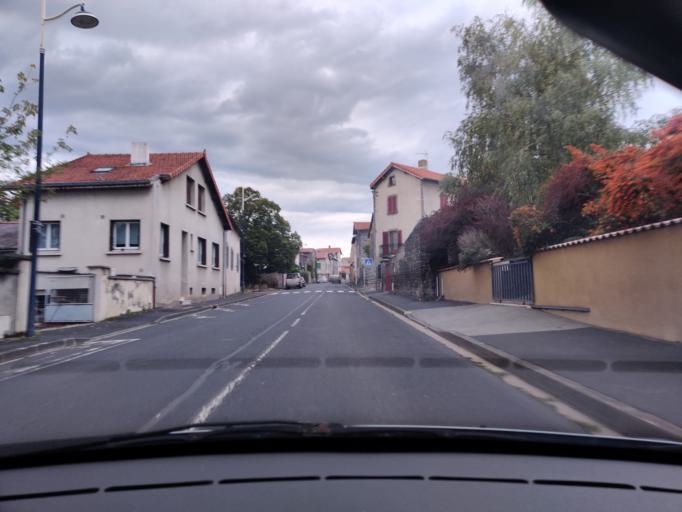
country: FR
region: Auvergne
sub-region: Departement du Puy-de-Dome
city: Saint-Bonnet-pres-Riom
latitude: 45.9257
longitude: 3.1164
